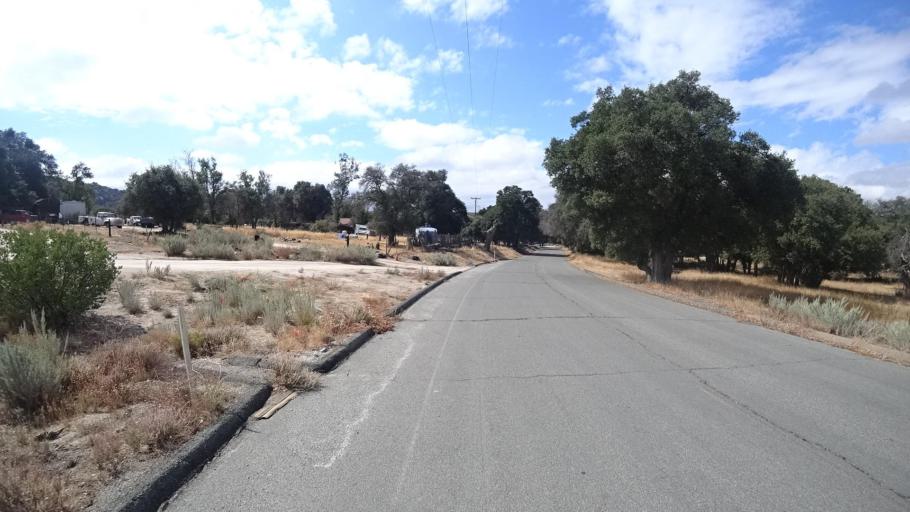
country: US
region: California
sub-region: San Diego County
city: Campo
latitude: 32.6933
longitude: -116.3326
